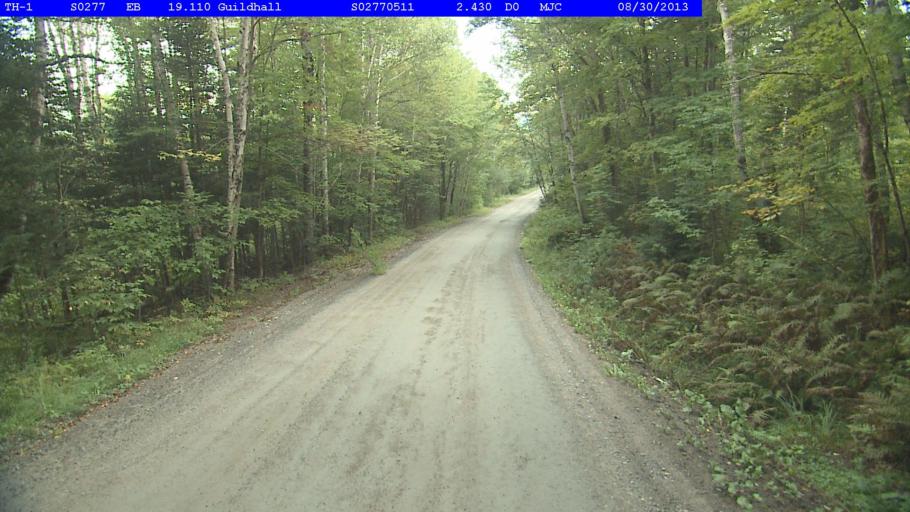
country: US
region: Vermont
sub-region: Essex County
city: Guildhall
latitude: 44.5601
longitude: -71.6273
